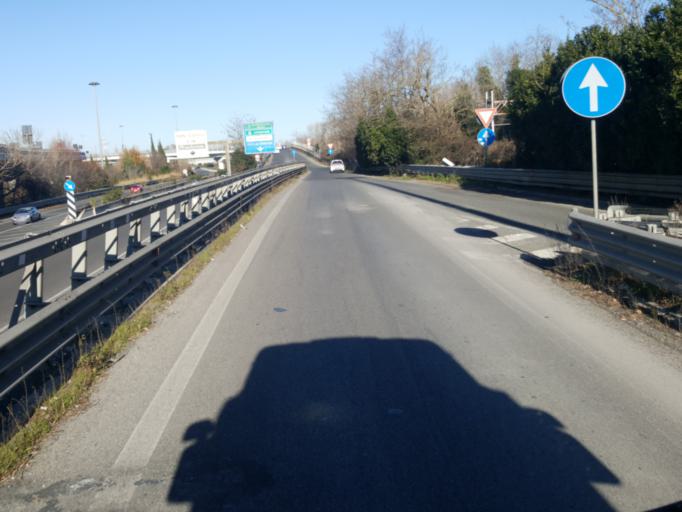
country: IT
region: Latium
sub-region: Citta metropolitana di Roma Capitale
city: Vitinia
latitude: 41.8006
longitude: 12.4178
